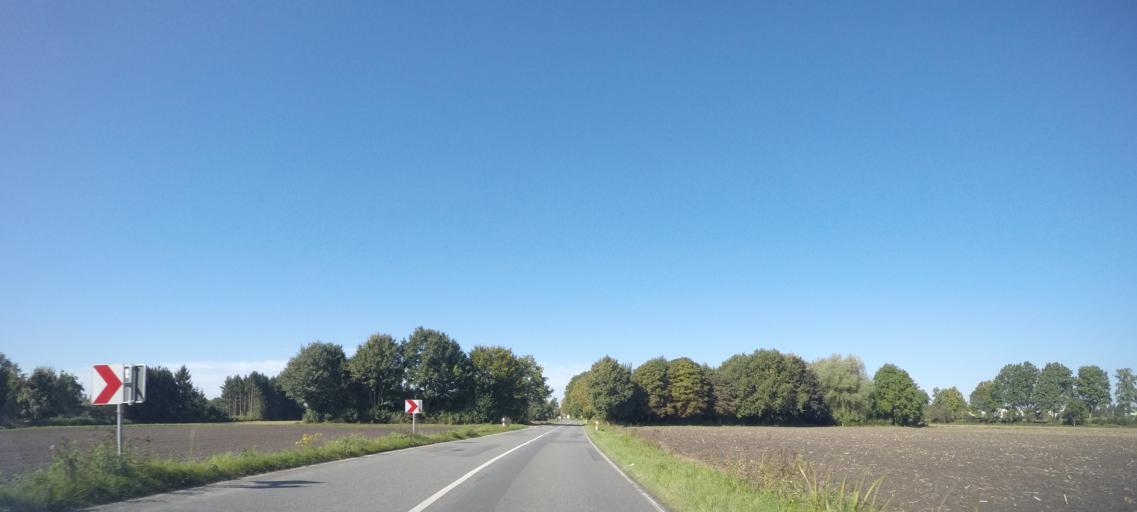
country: DE
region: North Rhine-Westphalia
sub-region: Regierungsbezirk Arnsberg
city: Bad Sassendorf
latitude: 51.6615
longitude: 8.1568
